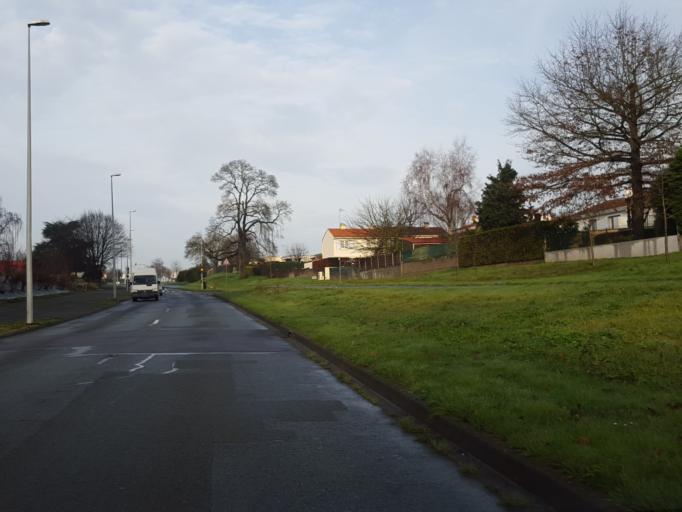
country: FR
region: Pays de la Loire
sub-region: Departement de la Vendee
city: La Roche-sur-Yon
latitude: 46.6812
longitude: -1.4224
